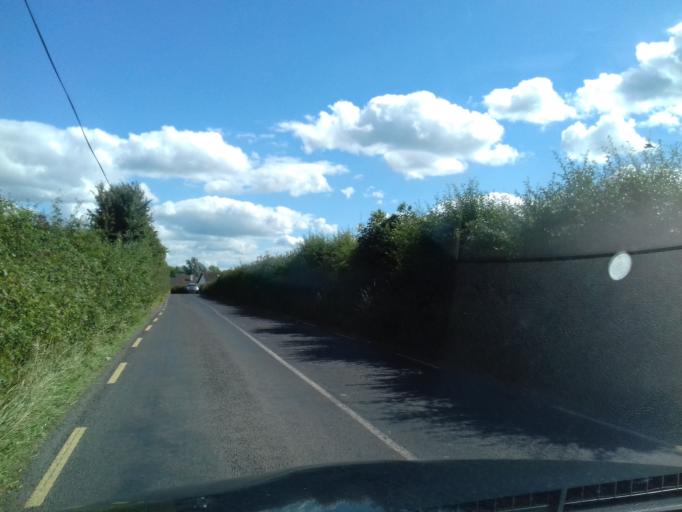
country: IE
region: Leinster
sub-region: Kilkenny
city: Callan
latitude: 52.5371
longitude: -7.3803
